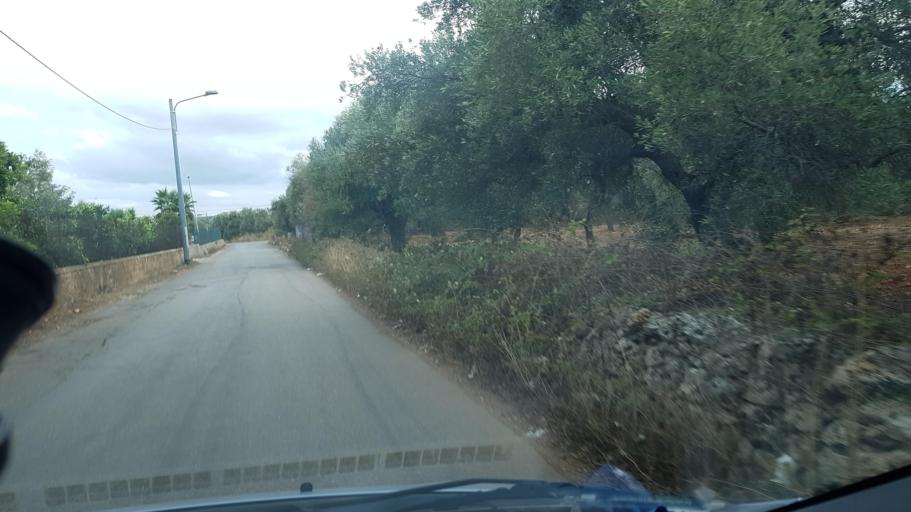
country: IT
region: Apulia
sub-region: Provincia di Brindisi
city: San Vito dei Normanni
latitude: 40.6622
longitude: 17.7165
